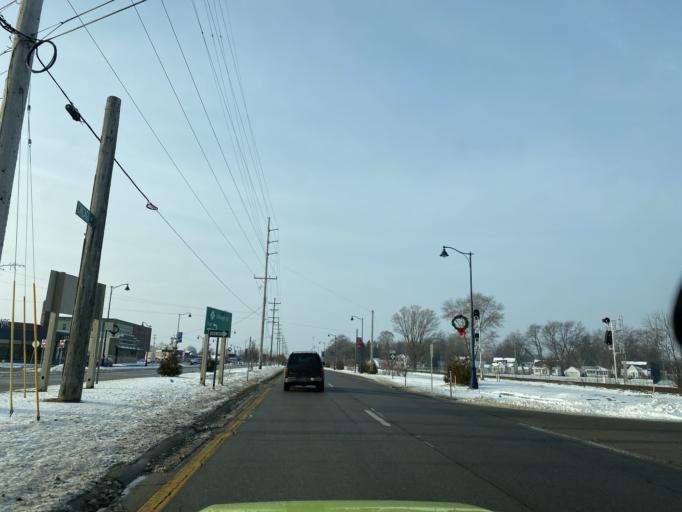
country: US
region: Michigan
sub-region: Ottawa County
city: Hudsonville
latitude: 42.8687
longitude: -85.8650
